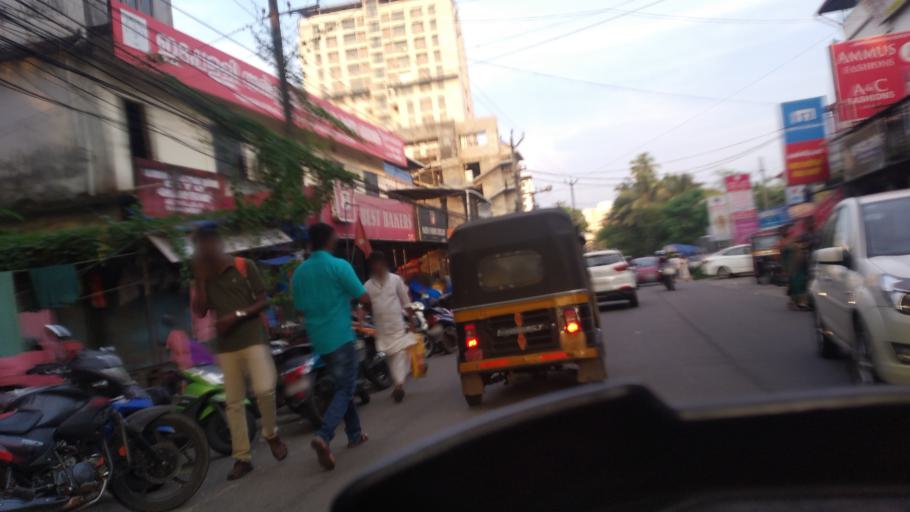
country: IN
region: Kerala
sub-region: Ernakulam
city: Elur
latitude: 10.0193
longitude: 76.2914
